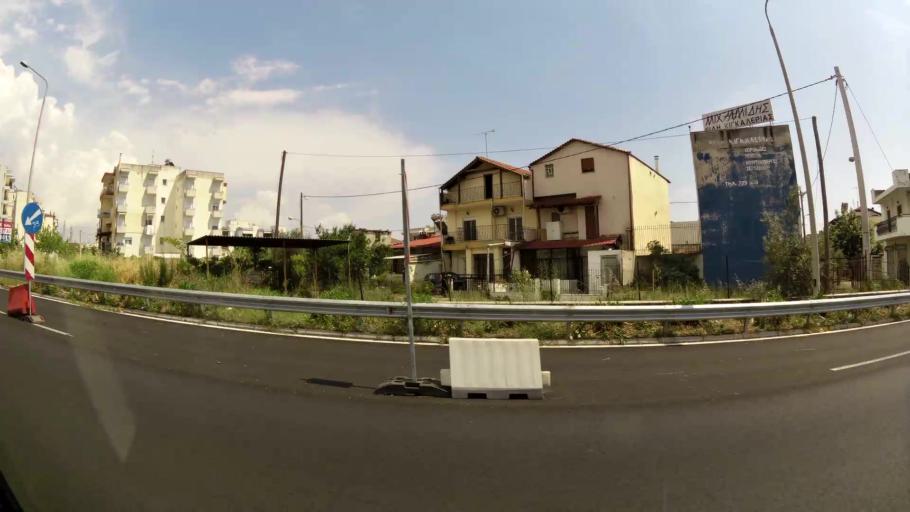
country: GR
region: Central Macedonia
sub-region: Nomos Thessalonikis
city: Evosmos
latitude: 40.6766
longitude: 22.8954
